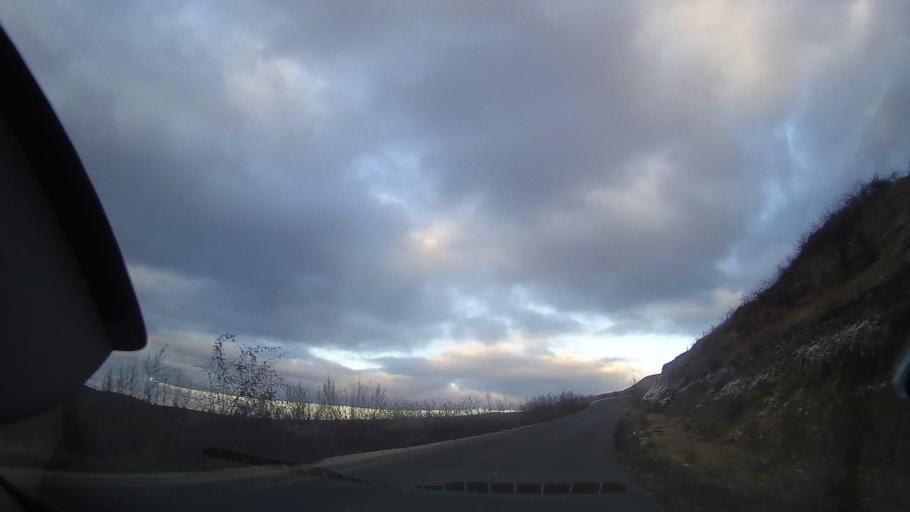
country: RO
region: Cluj
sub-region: Comuna Calatele
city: Calatele
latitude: 46.7824
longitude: 23.0473
